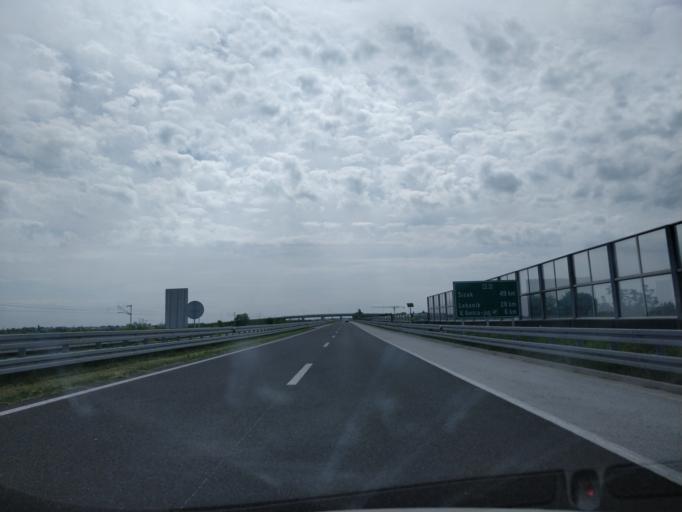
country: HR
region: Grad Zagreb
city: Odra
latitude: 45.7313
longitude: 16.0145
